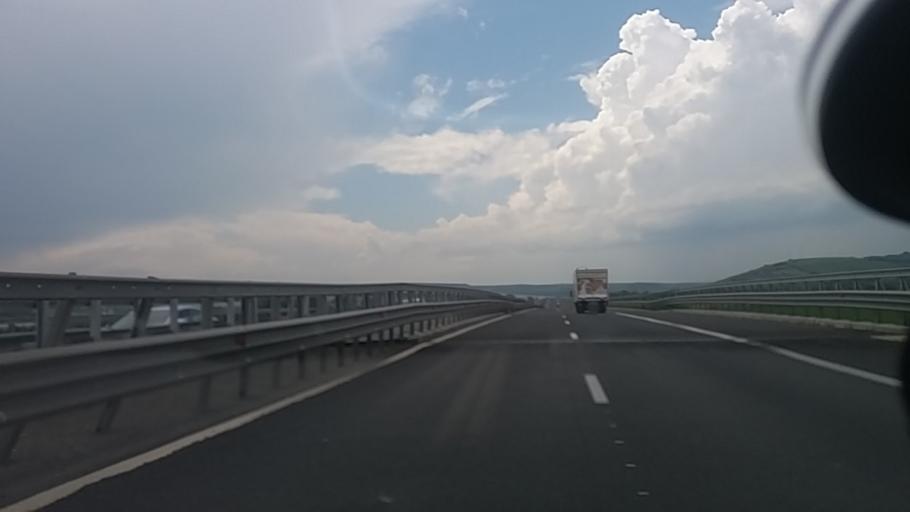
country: RO
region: Sibiu
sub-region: Oras Miercurea Sibiului
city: Miercurea Sibiului
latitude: 45.8969
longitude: 23.8001
